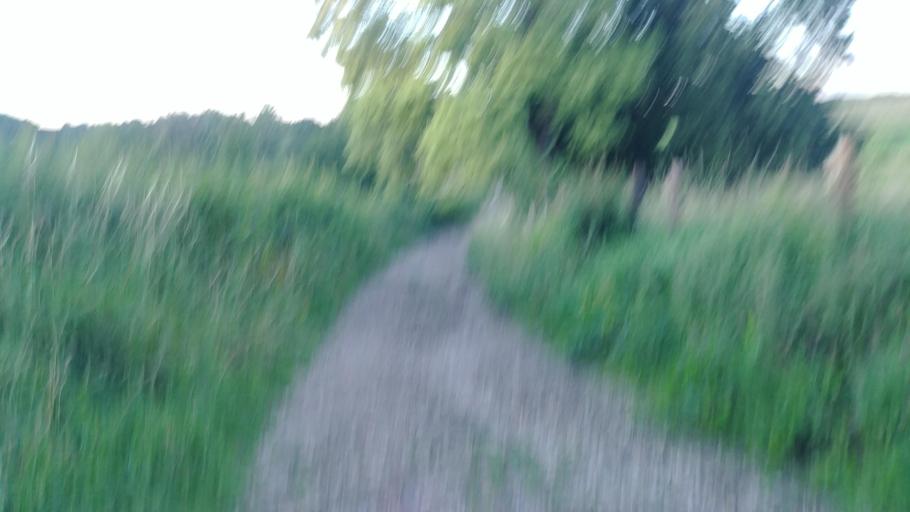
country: BE
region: Flanders
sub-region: Provincie Limburg
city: Sint-Pieters-Voeren
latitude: 50.7611
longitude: 5.7969
